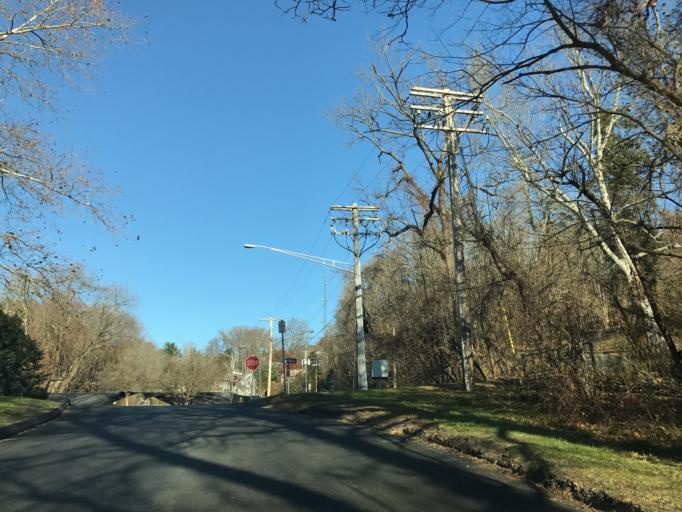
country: US
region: Maryland
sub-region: Howard County
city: Ellicott City
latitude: 39.2698
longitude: -76.8009
